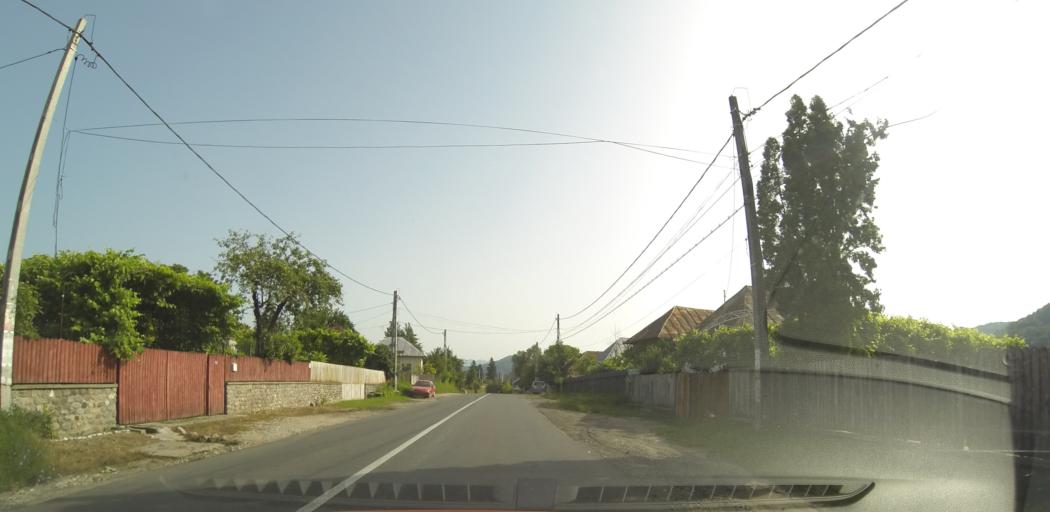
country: RO
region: Valcea
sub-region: Comuna Pausesti-Maglasi
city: Pausesti-Maglasi
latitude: 45.1502
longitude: 24.2460
